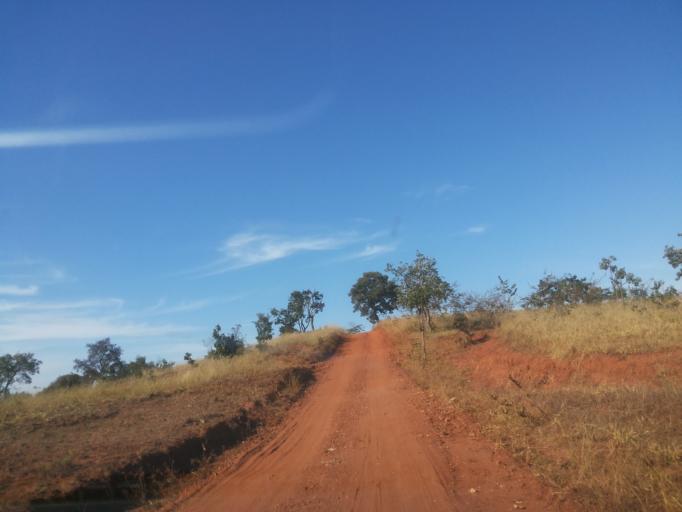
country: BR
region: Minas Gerais
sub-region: Ituiutaba
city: Ituiutaba
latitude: -19.1046
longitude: -49.4172
